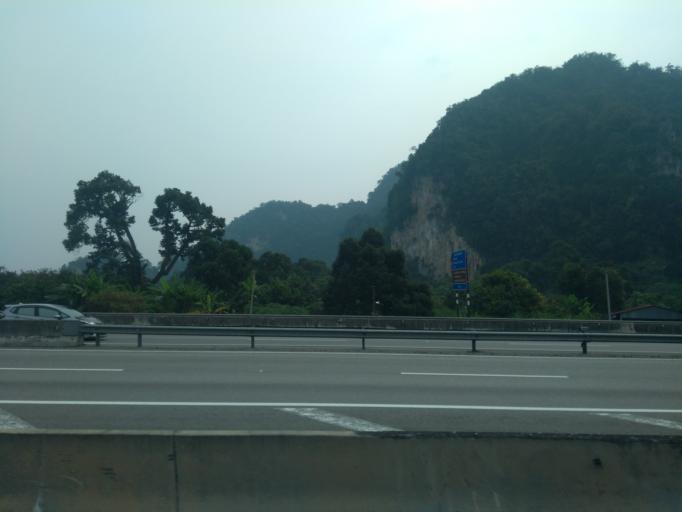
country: MY
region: Perak
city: Ipoh
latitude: 4.5973
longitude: 101.1423
